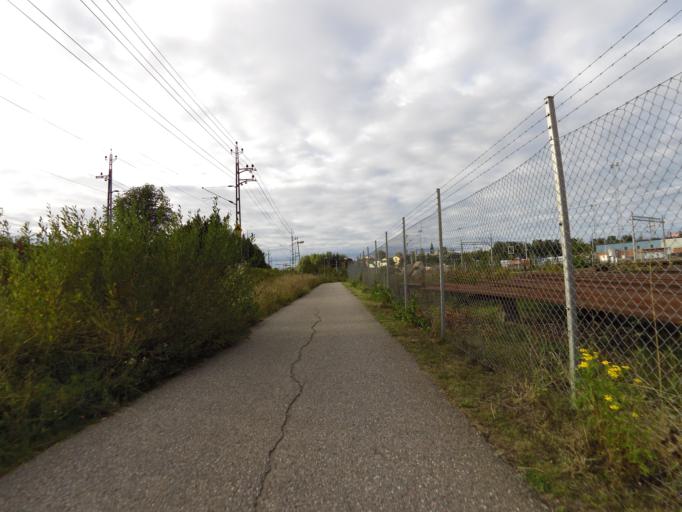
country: SE
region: Gaevleborg
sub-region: Gavle Kommun
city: Gavle
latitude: 60.6647
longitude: 17.1668
